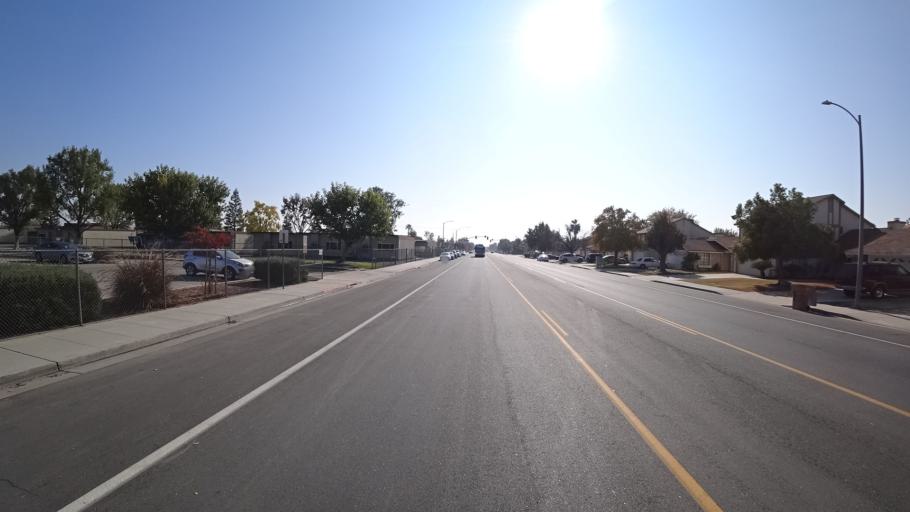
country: US
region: California
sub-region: Kern County
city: Greenfield
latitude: 35.3045
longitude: -119.0119
